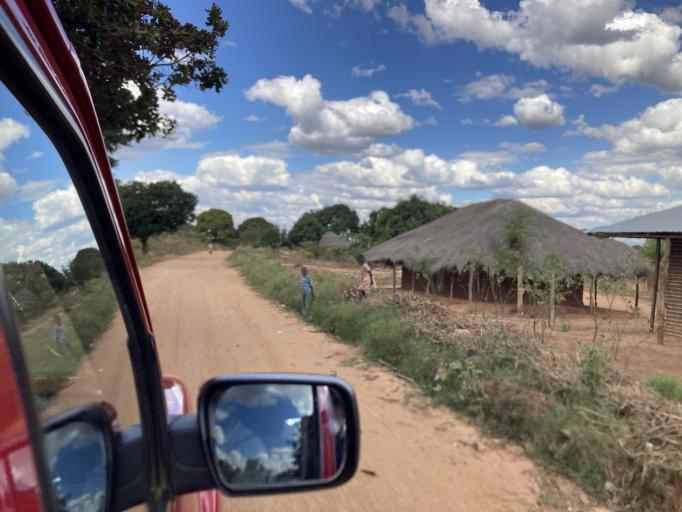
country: MZ
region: Cabo Delgado
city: Montepuez
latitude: -13.1255
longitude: 39.0297
